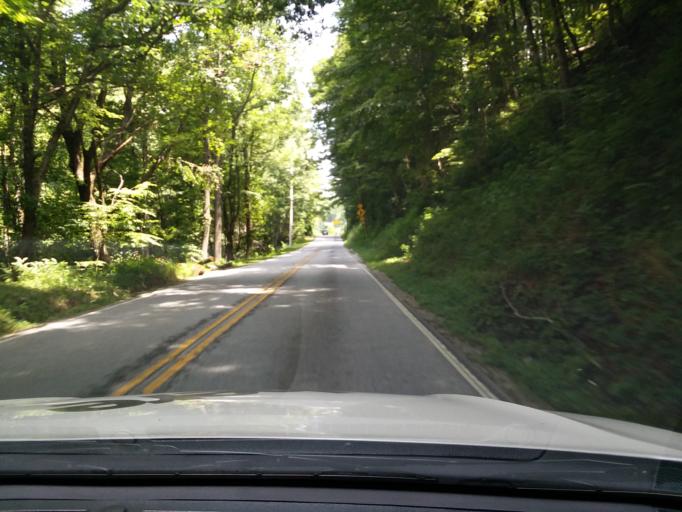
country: US
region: Georgia
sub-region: Rabun County
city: Mountain City
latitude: 34.9978
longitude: -83.3358
